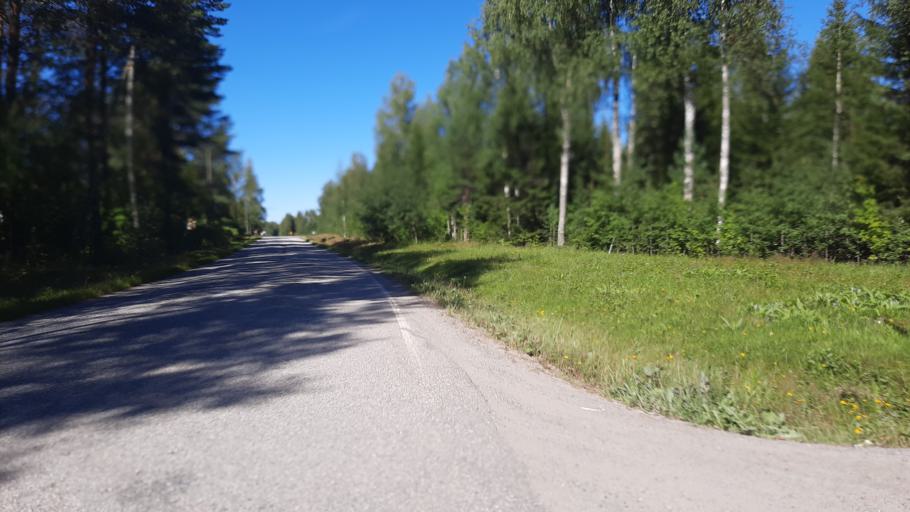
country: FI
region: North Karelia
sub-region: Joensuu
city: Joensuu
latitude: 62.6298
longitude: 29.7355
